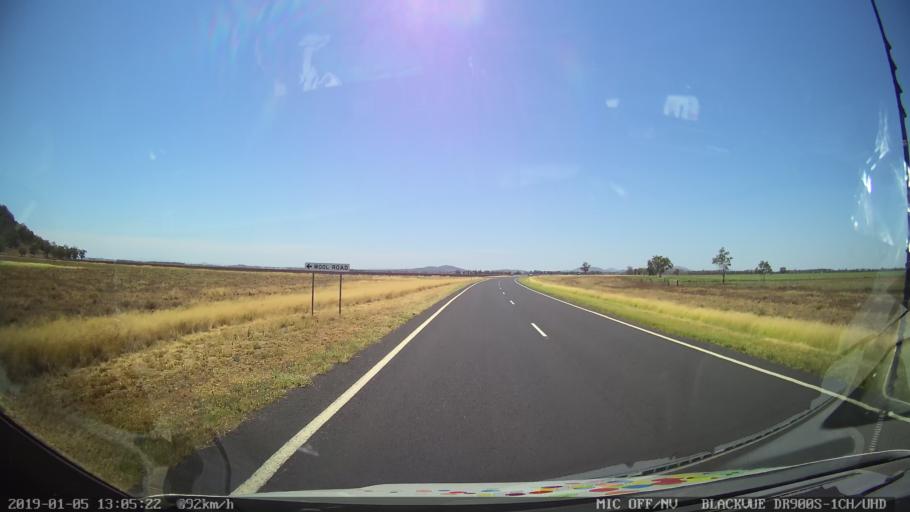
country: AU
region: New South Wales
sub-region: Gunnedah
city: Gunnedah
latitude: -31.0959
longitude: 149.8523
